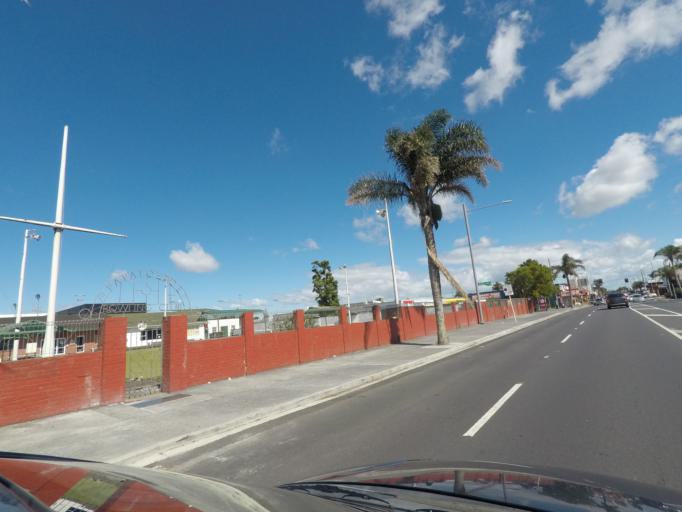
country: NZ
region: Auckland
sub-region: Auckland
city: Wiri
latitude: -36.9719
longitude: 174.8628
